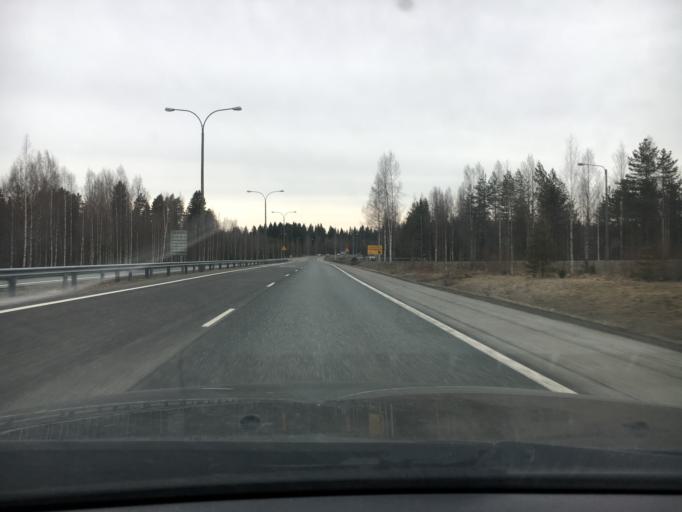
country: FI
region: Northern Savo
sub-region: Kuopio
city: Siilinjaervi
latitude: 63.0800
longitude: 27.6482
